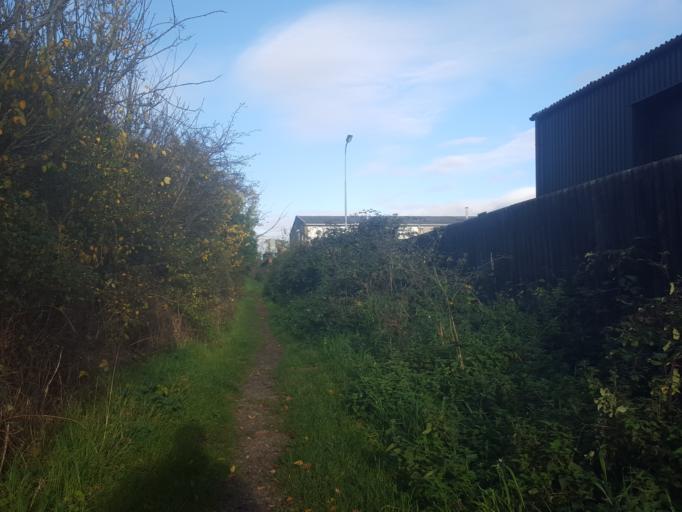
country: GB
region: England
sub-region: Essex
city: Little Clacton
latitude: 51.8166
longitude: 1.1687
